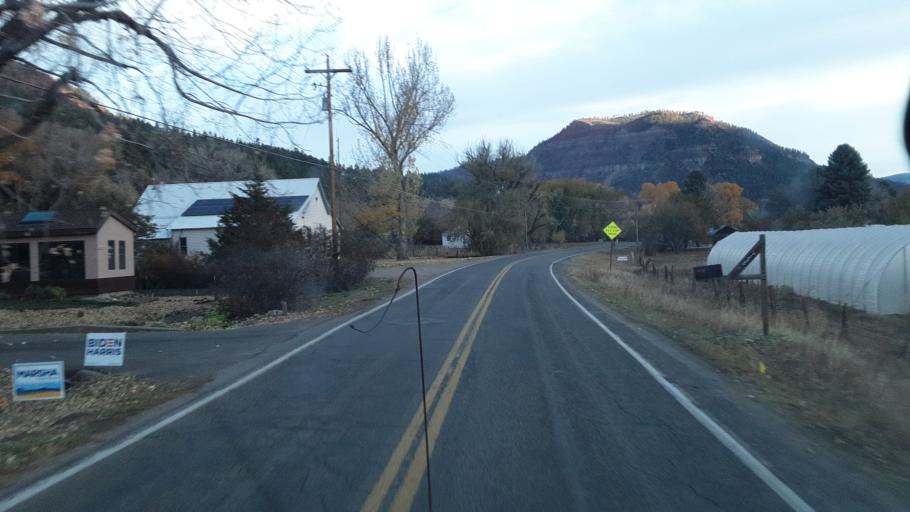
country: US
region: Colorado
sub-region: La Plata County
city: Durango
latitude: 37.4024
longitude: -107.8463
